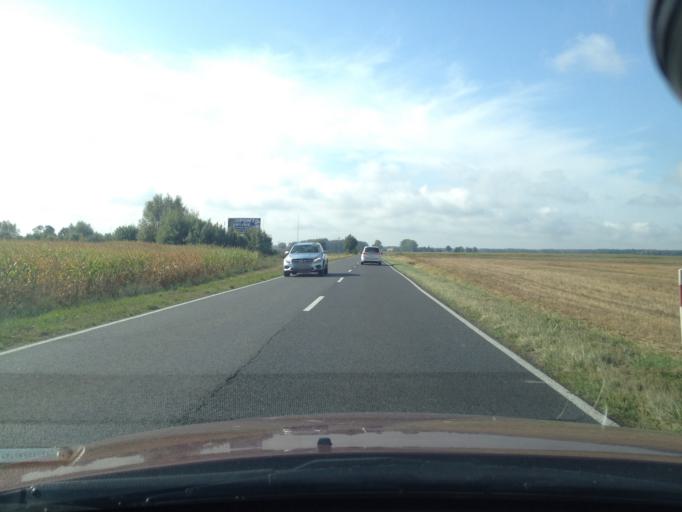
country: PL
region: West Pomeranian Voivodeship
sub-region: Powiat kamienski
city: Kamien Pomorski
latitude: 53.9038
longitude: 14.7977
